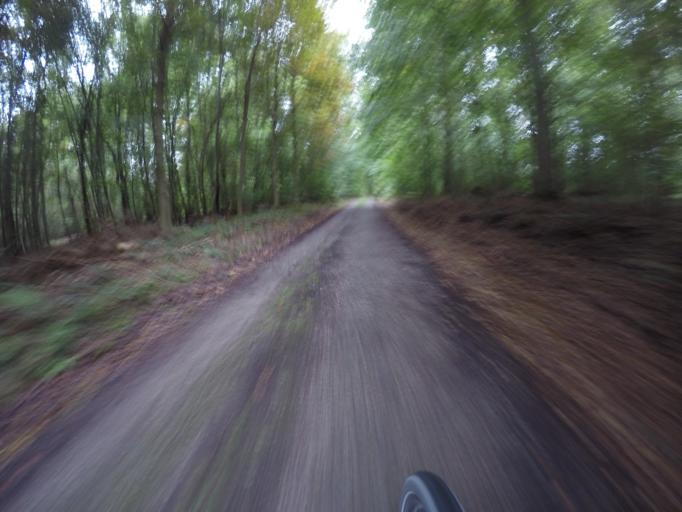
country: DE
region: Baden-Wuerttemberg
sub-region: Regierungsbezirk Stuttgart
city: Gerlingen
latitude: 48.7568
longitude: 9.0499
